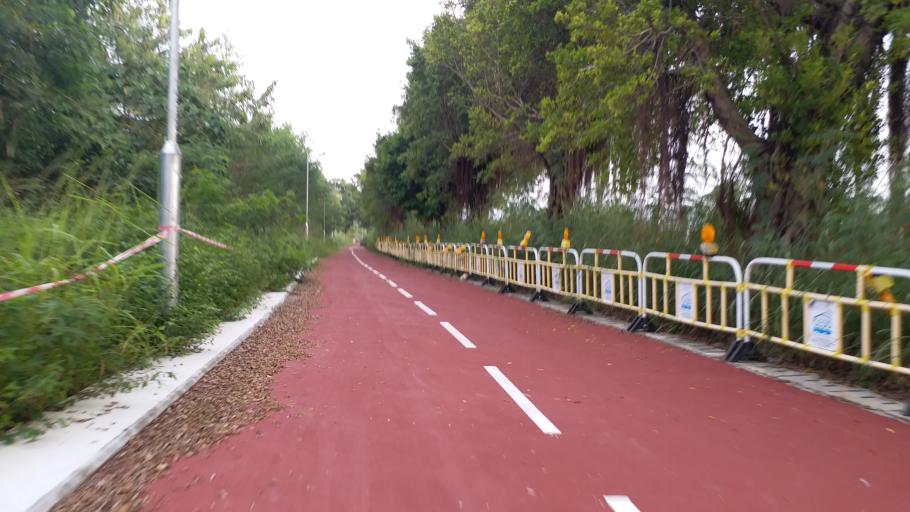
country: HK
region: Yuen Long
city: Yuen Long Kau Hui
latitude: 22.4633
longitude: 114.0453
